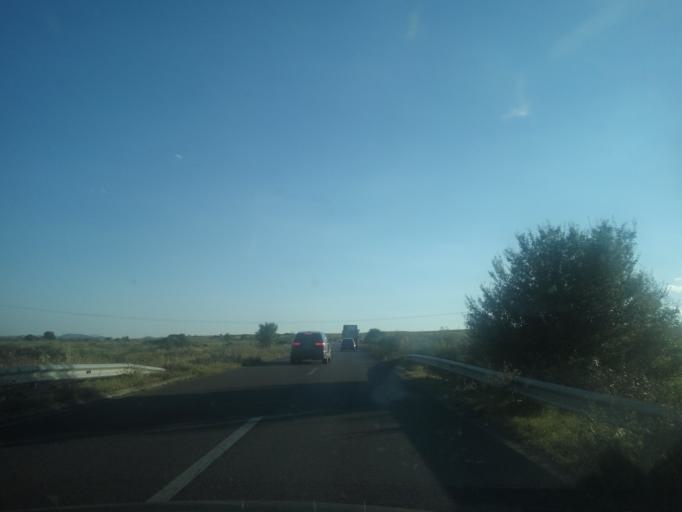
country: XK
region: Gjakova
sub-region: Komuna e Gjakoves
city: Gjakove
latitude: 42.4503
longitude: 20.4972
